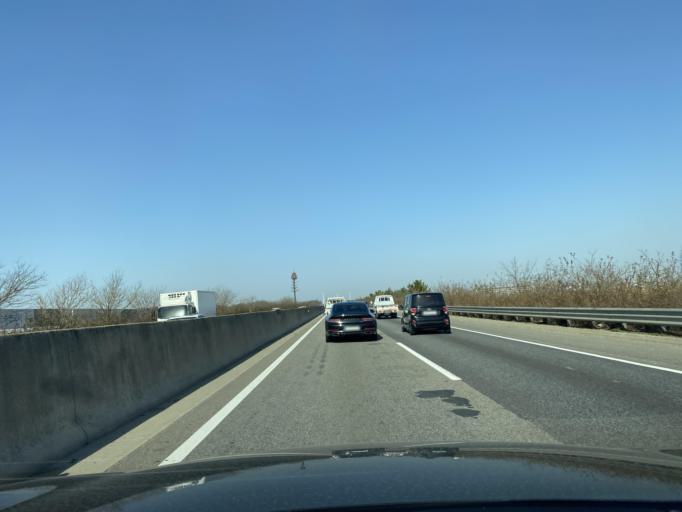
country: KR
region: Gyeonggi-do
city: Hwaseong-si
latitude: 37.2677
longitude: 126.7459
